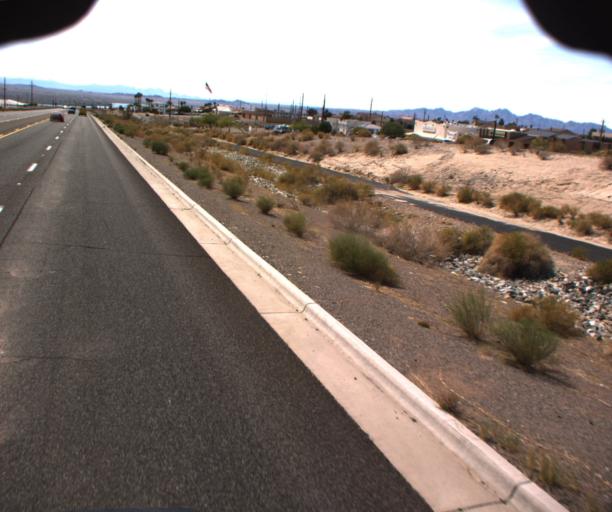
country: US
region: Arizona
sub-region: Mohave County
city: Lake Havasu City
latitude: 34.4557
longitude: -114.2915
